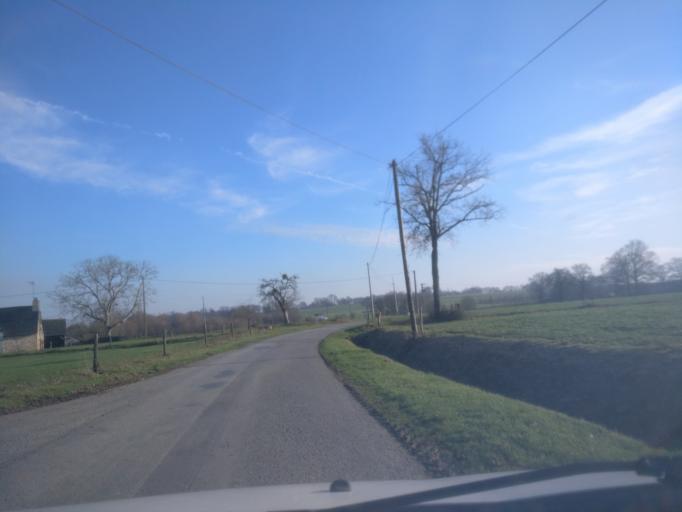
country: FR
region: Brittany
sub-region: Departement d'Ille-et-Vilaine
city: Livre-sur-Changeon
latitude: 48.2158
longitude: -1.3093
